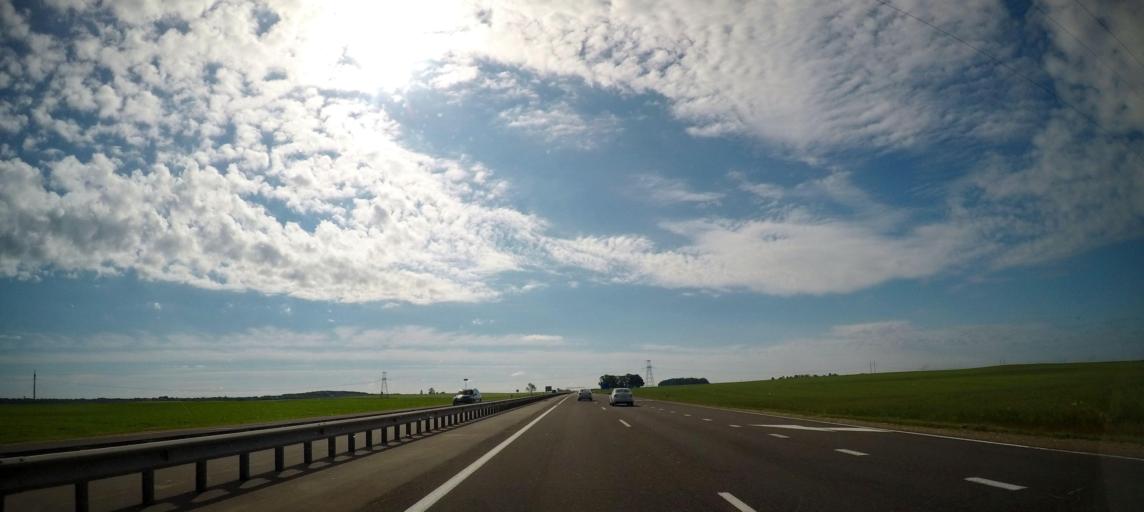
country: BY
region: Grodnenskaya
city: Hrodna
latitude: 53.6420
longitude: 24.0115
